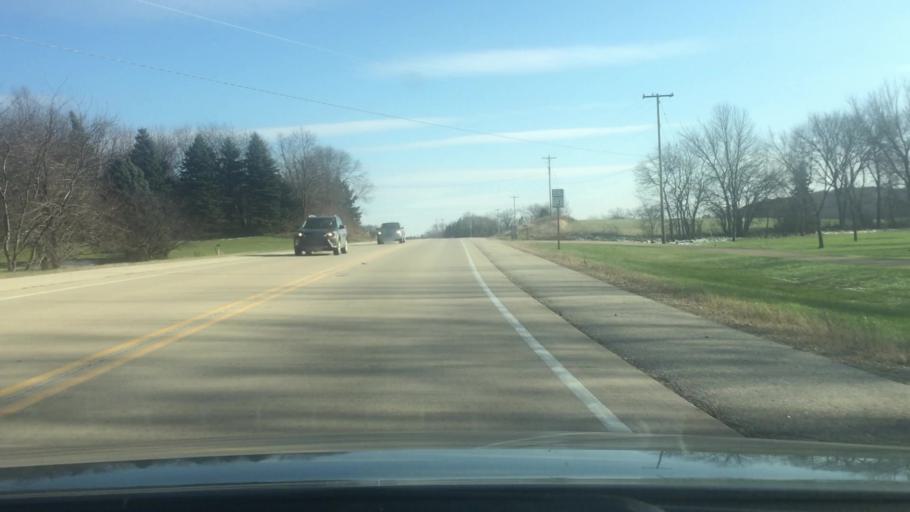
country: US
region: Wisconsin
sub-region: Jefferson County
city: Lake Koshkonong
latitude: 42.9714
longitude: -88.9182
